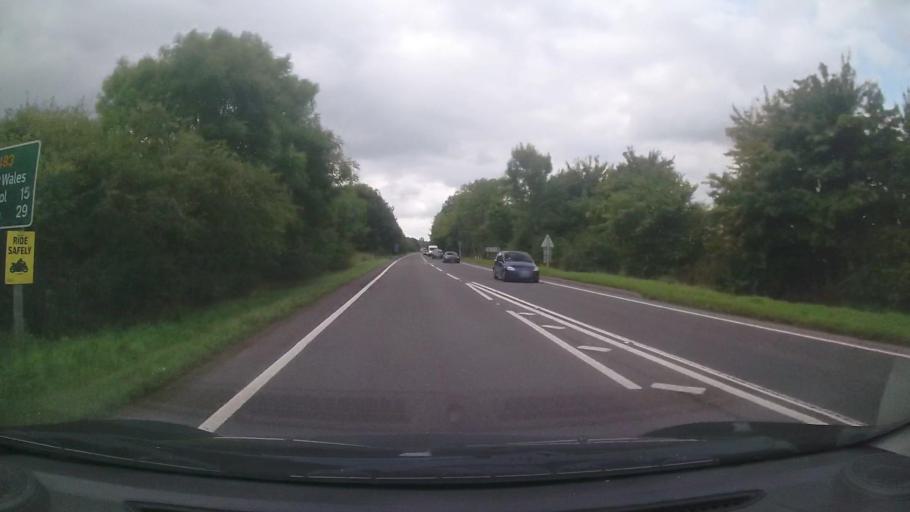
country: GB
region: England
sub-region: Shropshire
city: Oswestry
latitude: 52.8476
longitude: -3.0298
